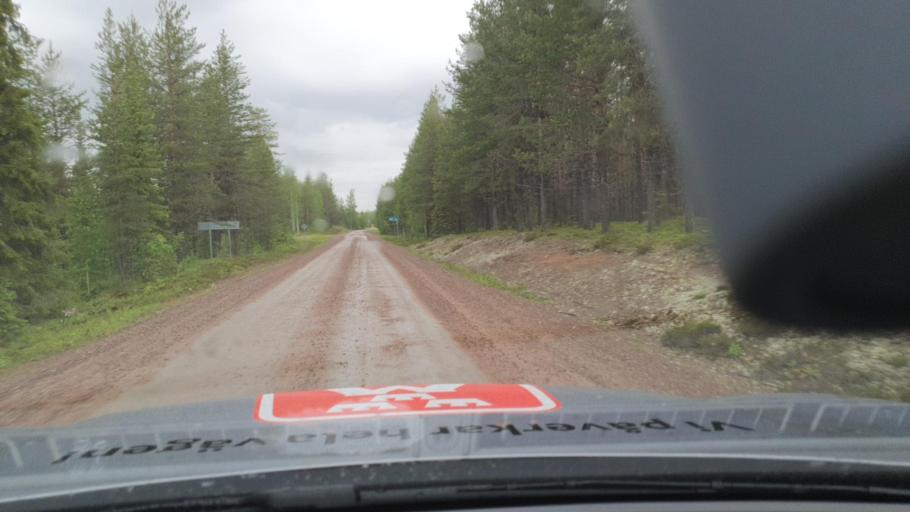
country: SE
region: Norrbotten
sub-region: Overkalix Kommun
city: OEverkalix
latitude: 66.6454
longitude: 22.7000
